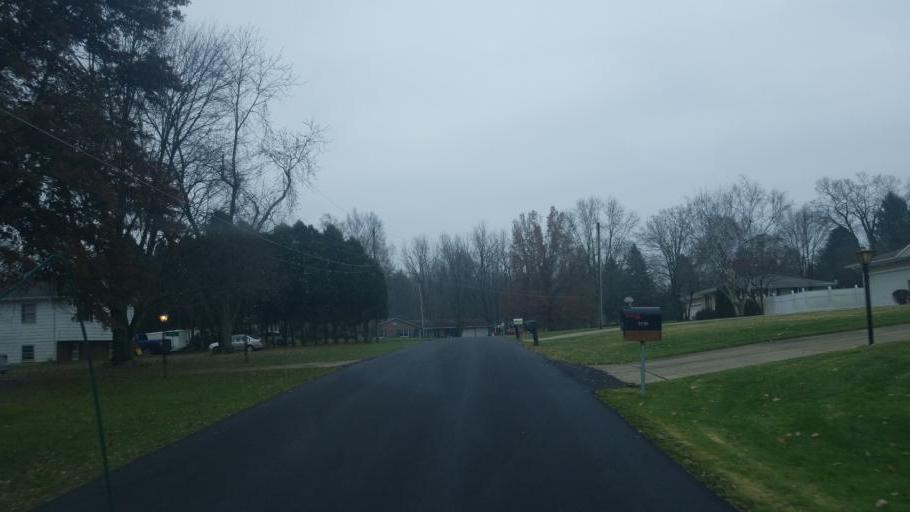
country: US
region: Ohio
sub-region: Richland County
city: Lexington
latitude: 40.6982
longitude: -82.5254
